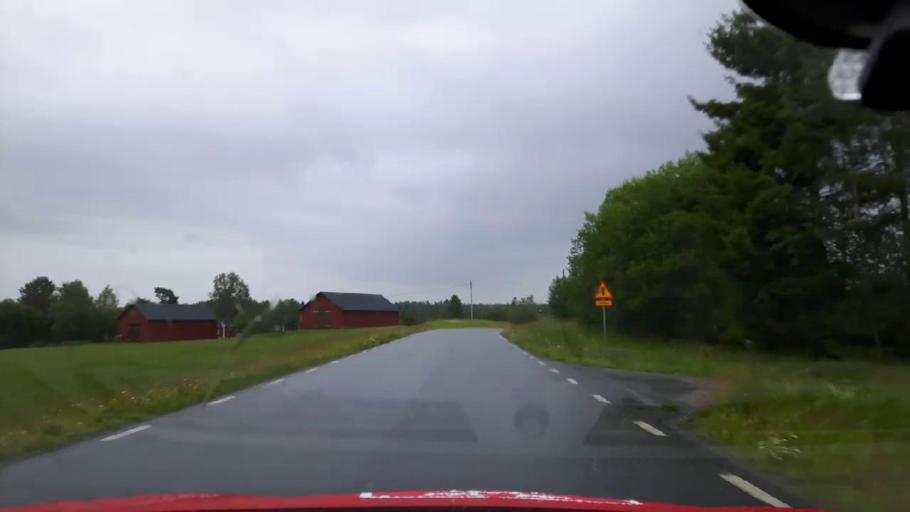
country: SE
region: Jaemtland
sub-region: OEstersunds Kommun
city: Brunflo
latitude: 63.0126
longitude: 14.7330
